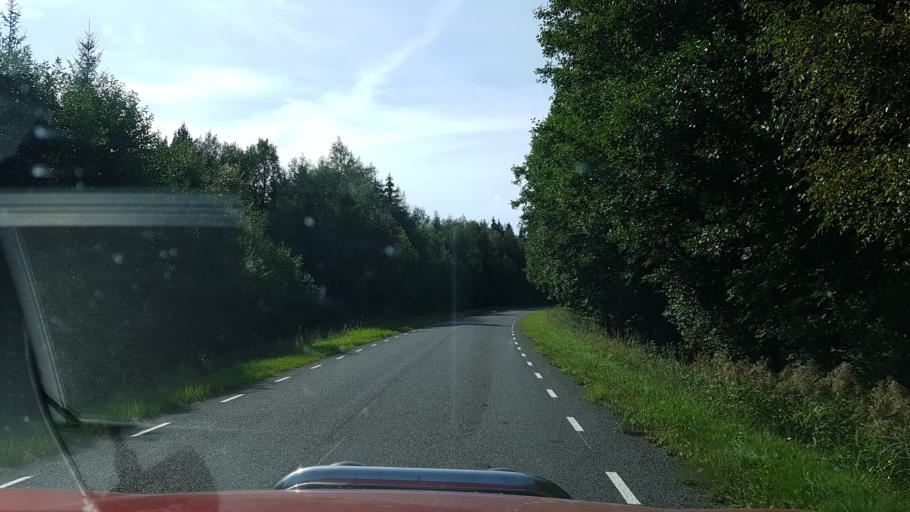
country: EE
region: Viljandimaa
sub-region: Moisakuela linn
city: Moisakula
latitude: 58.3325
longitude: 25.2056
